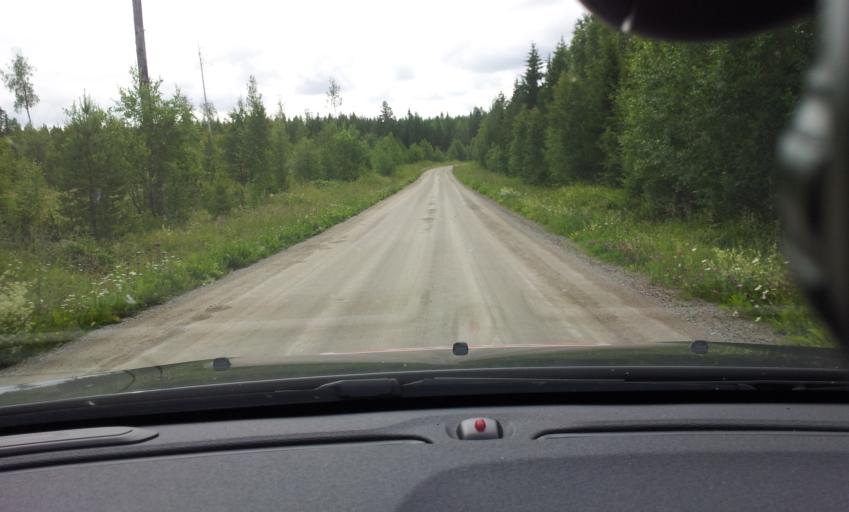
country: SE
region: Jaemtland
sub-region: OEstersunds Kommun
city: Brunflo
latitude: 62.9661
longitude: 14.9058
